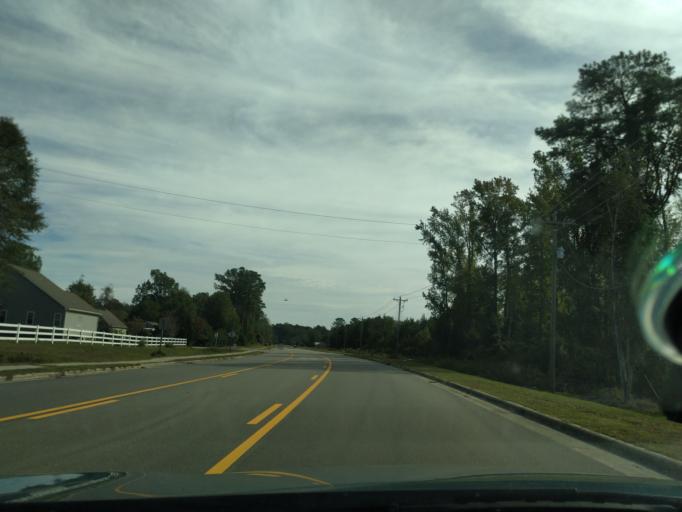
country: US
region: North Carolina
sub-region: Beaufort County
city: River Road
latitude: 35.5146
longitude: -77.0040
